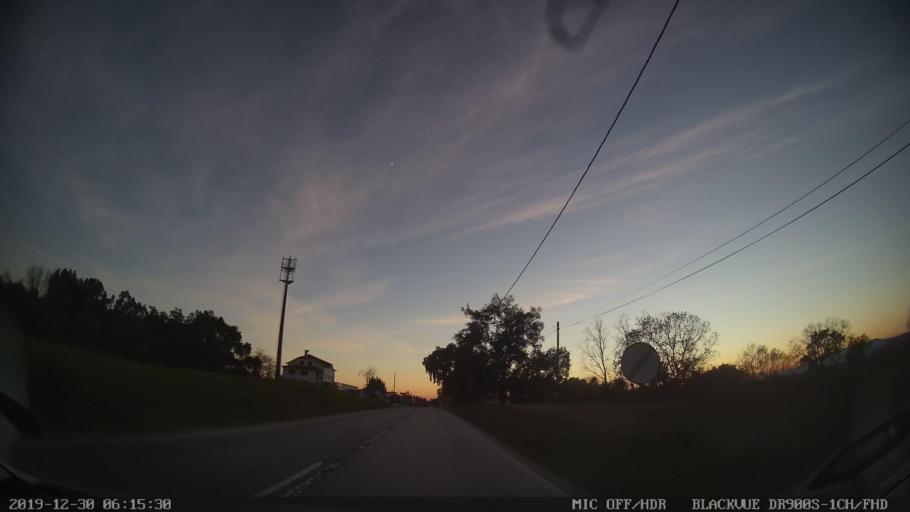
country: PT
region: Castelo Branco
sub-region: Penamacor
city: Penamacor
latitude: 40.1103
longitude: -7.2226
